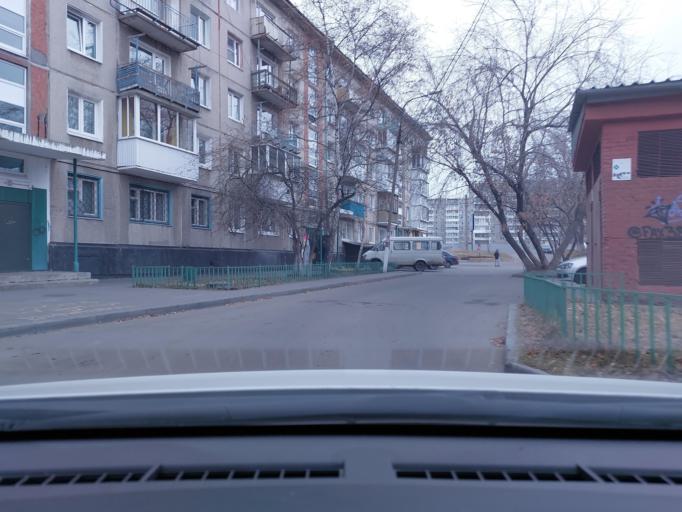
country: RU
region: Irkutsk
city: Smolenshchina
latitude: 52.3487
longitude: 104.1661
